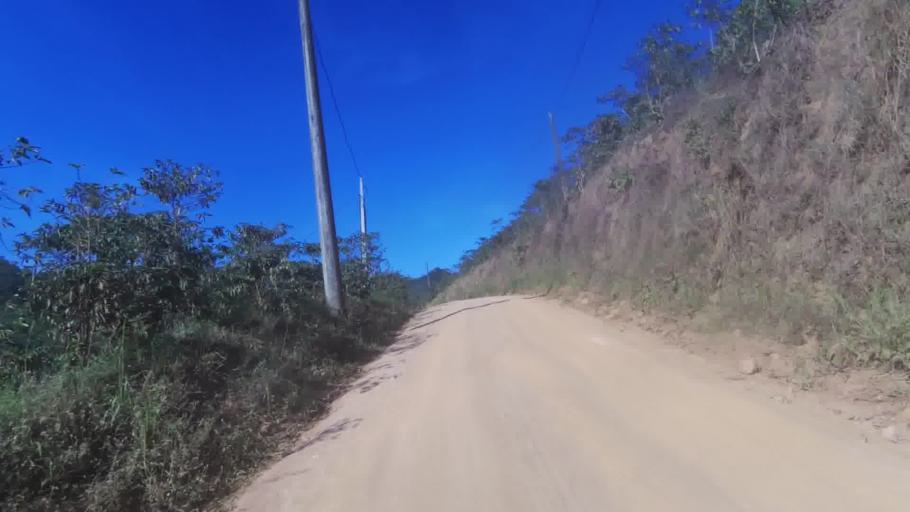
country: BR
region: Espirito Santo
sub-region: Iconha
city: Iconha
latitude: -20.7622
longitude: -40.8274
